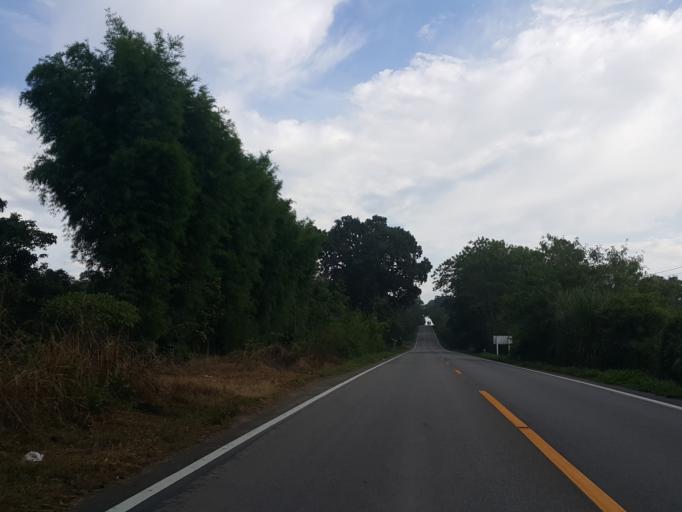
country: TH
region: Chiang Mai
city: Phrao
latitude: 19.2692
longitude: 99.1873
